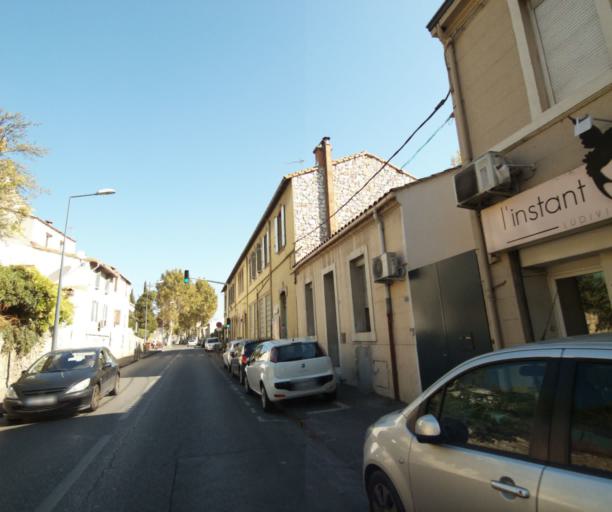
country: FR
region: Provence-Alpes-Cote d'Azur
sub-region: Departement des Bouches-du-Rhone
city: Plan-de-Cuques
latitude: 43.3360
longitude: 5.4516
